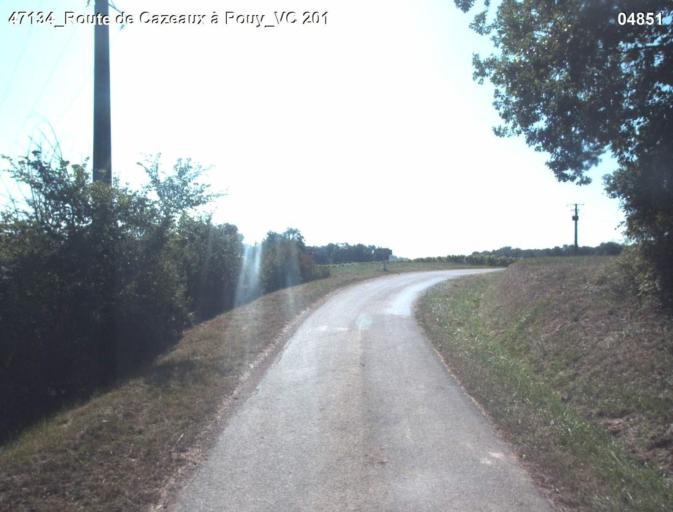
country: FR
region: Aquitaine
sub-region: Departement du Lot-et-Garonne
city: Mezin
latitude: 44.0394
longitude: 0.3130
